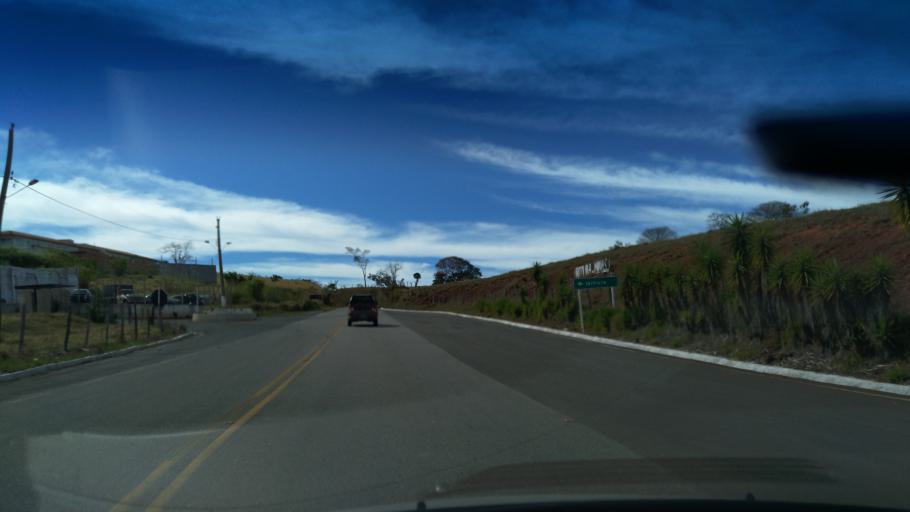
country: BR
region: Minas Gerais
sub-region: Andradas
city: Andradas
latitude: -22.0691
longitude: -46.4440
